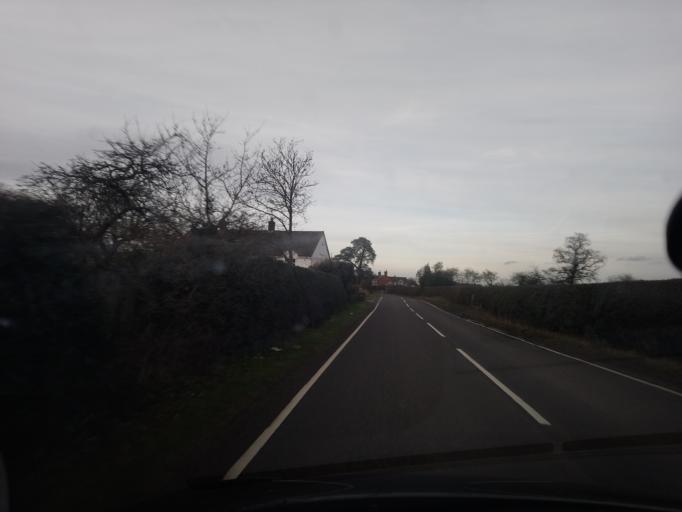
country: GB
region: England
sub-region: Shropshire
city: Prees
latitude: 52.9179
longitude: -2.6825
